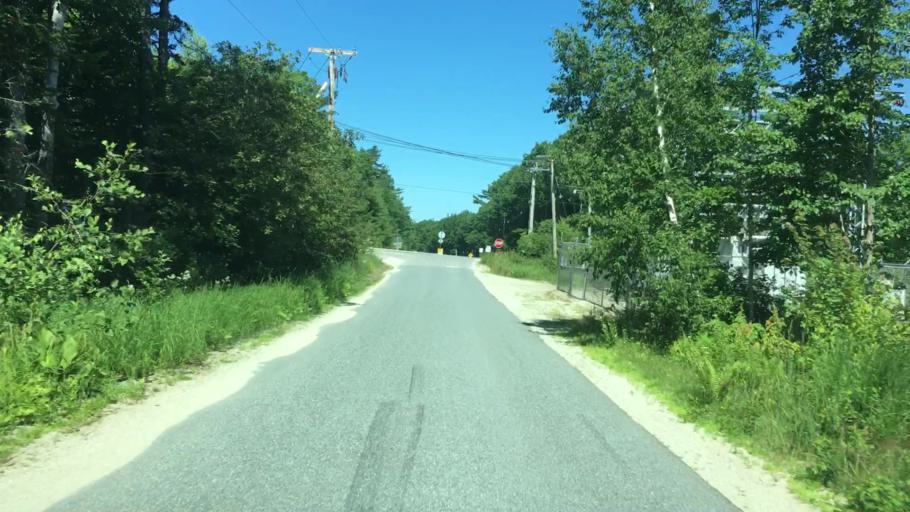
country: US
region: Maine
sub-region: Hancock County
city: Sedgwick
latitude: 44.3421
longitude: -68.6730
